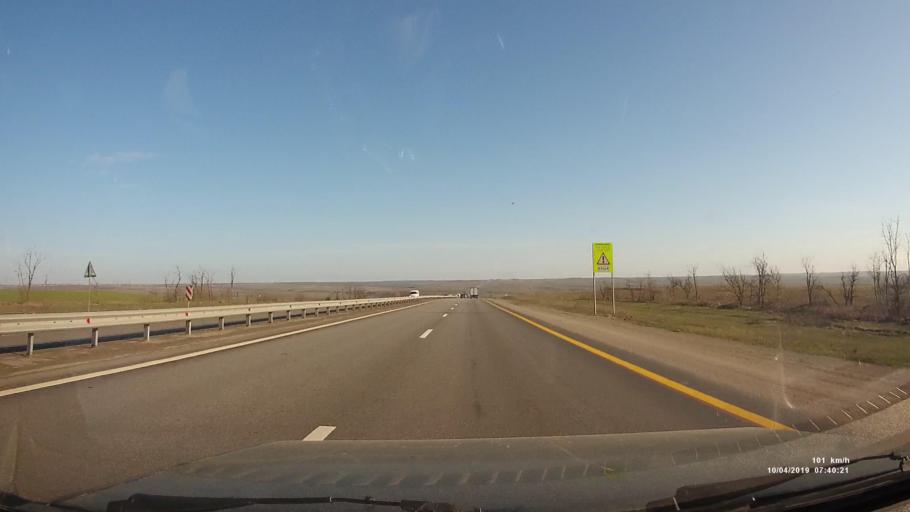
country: RU
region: Rostov
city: Likhoy
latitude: 48.1184
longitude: 40.2593
